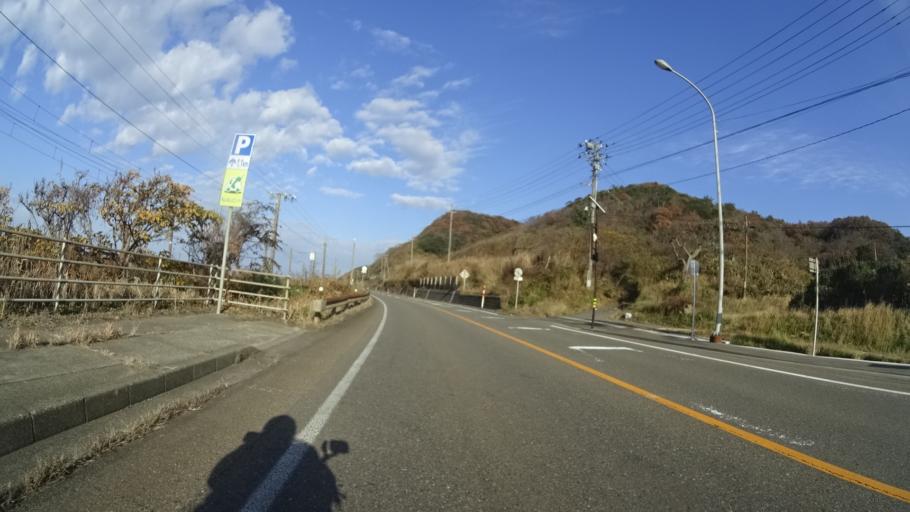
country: JP
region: Niigata
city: Kashiwazaki
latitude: 37.2976
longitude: 138.4092
